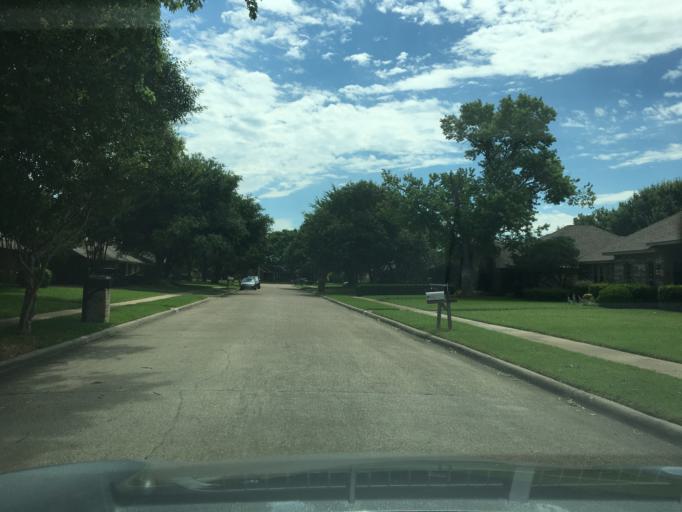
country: US
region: Texas
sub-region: Dallas County
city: Richardson
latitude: 32.9415
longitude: -96.7021
